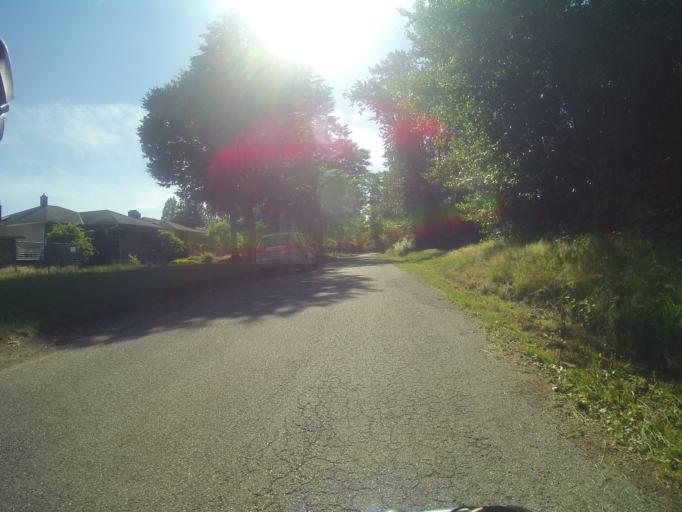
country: CA
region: British Columbia
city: Vancouver
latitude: 49.2178
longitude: -123.1147
